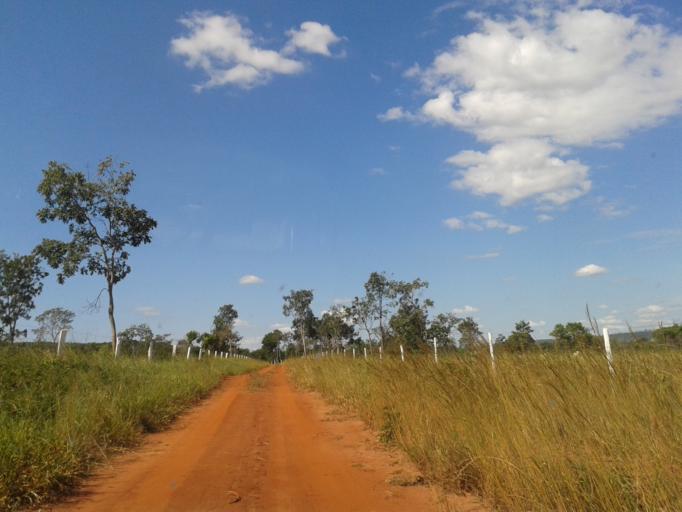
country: BR
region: Minas Gerais
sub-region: Campina Verde
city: Campina Verde
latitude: -19.3853
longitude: -49.7473
